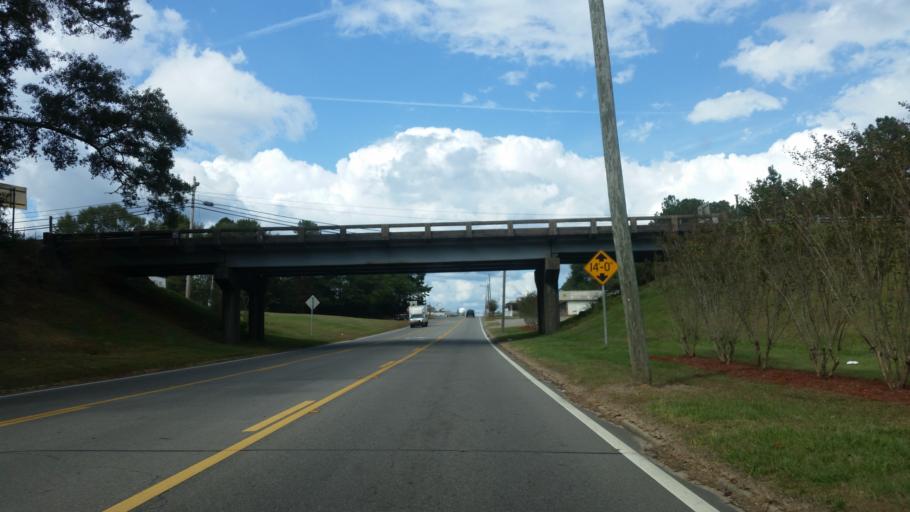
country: US
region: Mississippi
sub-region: Stone County
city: Wiggins
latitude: 30.8514
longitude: -89.1384
